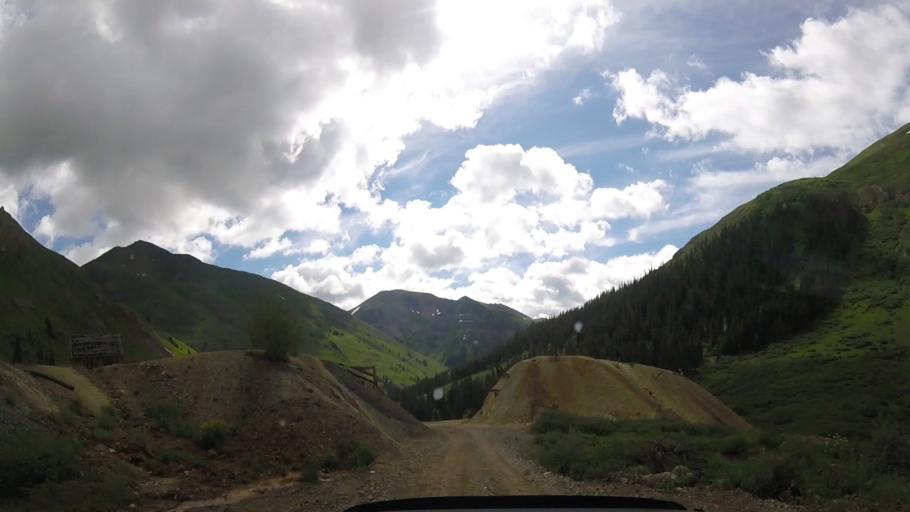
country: US
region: Colorado
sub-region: Ouray County
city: Ouray
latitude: 37.9323
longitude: -107.5818
